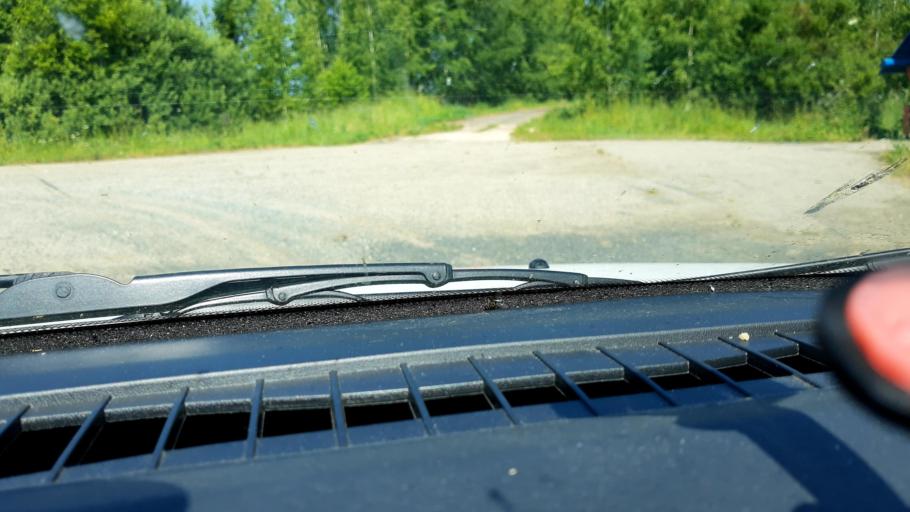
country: RU
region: Nizjnij Novgorod
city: Sharanga
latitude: 57.0683
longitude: 46.6849
